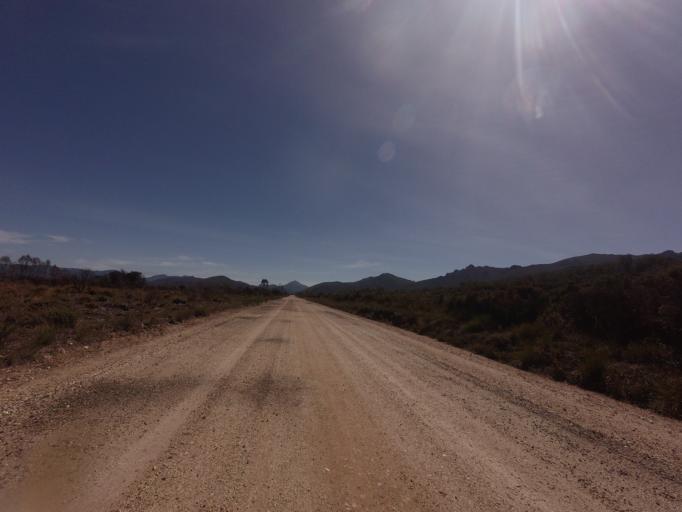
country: AU
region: Tasmania
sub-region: Huon Valley
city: Geeveston
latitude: -42.9719
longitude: 146.3646
